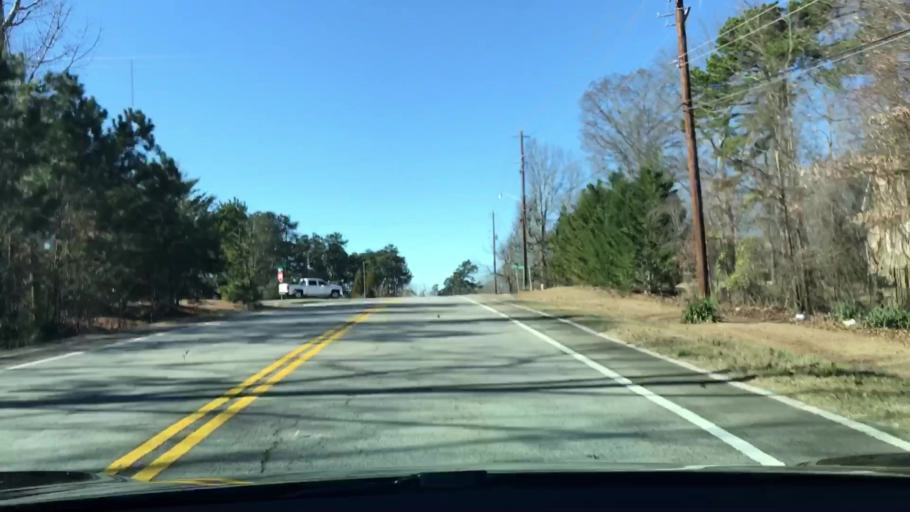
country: US
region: Georgia
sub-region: Gwinnett County
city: Buford
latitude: 34.1431
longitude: -83.9965
